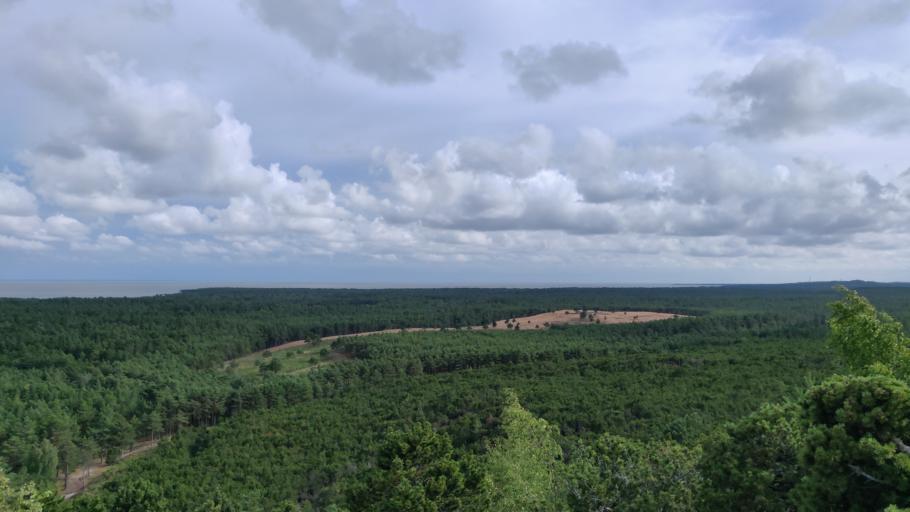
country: LT
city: Neringa
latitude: 55.3546
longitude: 21.0397
